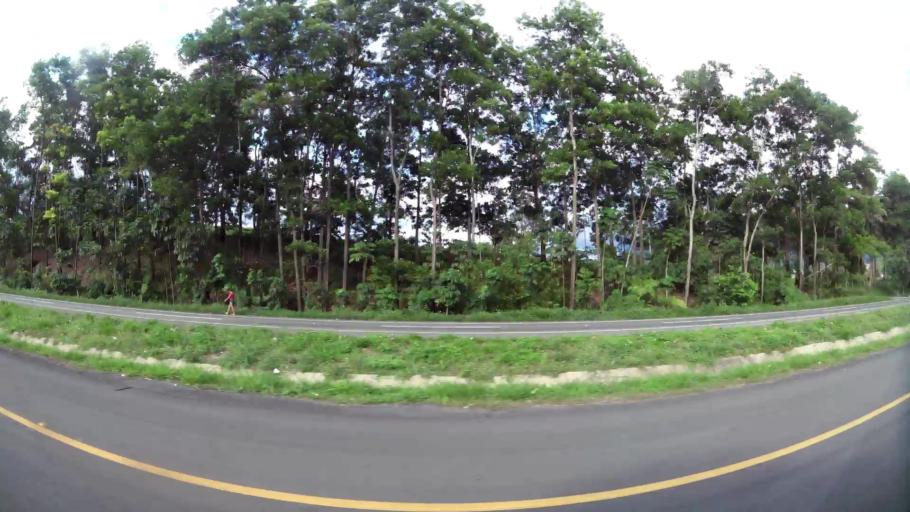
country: DO
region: Monsenor Nouel
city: Piedra Blanca
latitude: 18.8478
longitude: -70.3240
